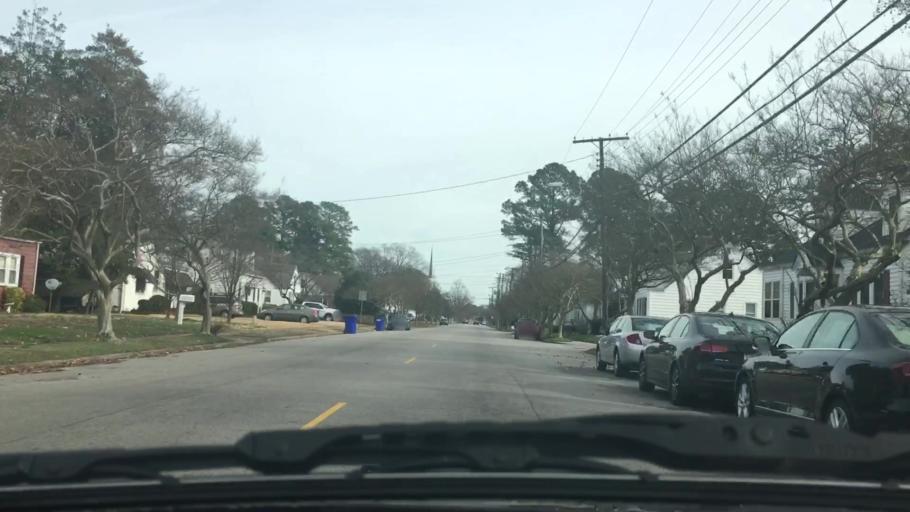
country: US
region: Virginia
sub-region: City of Norfolk
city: Norfolk
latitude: 36.8899
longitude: -76.2473
